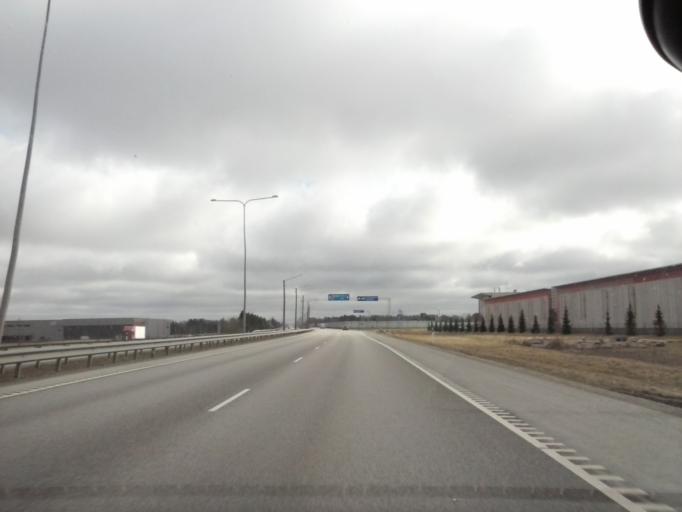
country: EE
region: Harju
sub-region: Rae vald
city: Jueri
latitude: 59.3829
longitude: 24.8369
